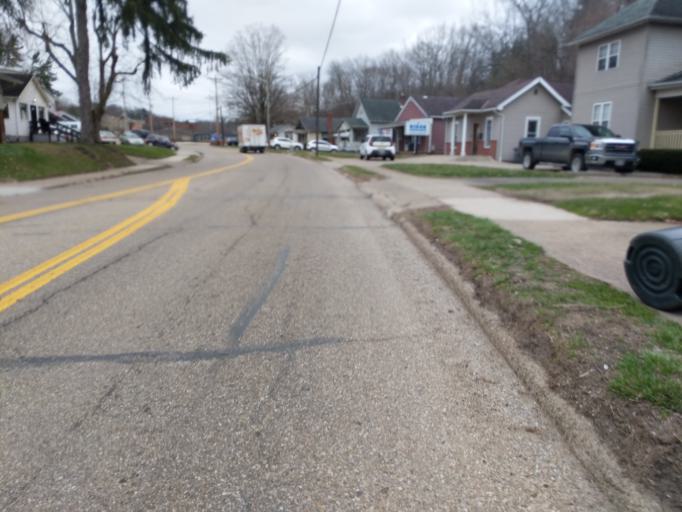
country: US
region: Ohio
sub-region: Athens County
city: Athens
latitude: 39.3093
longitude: -82.1046
